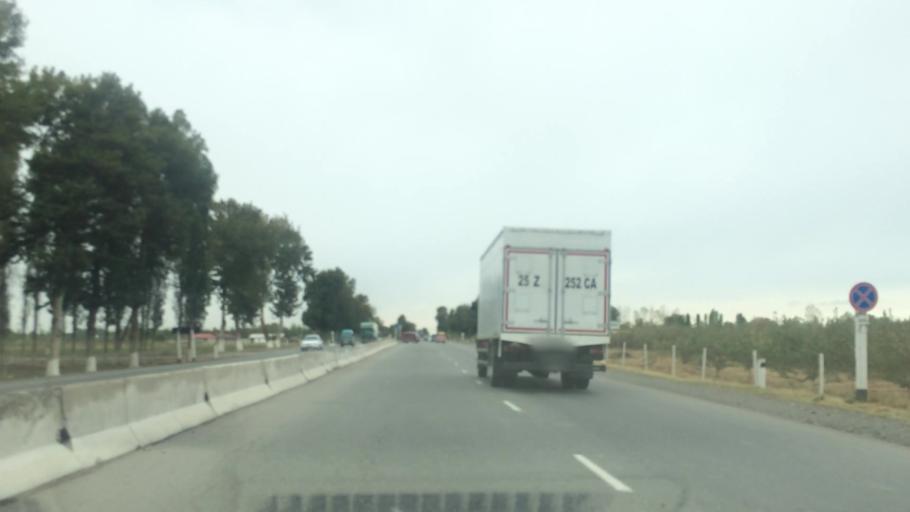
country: UZ
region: Samarqand
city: Jomboy
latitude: 39.7325
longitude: 67.1607
